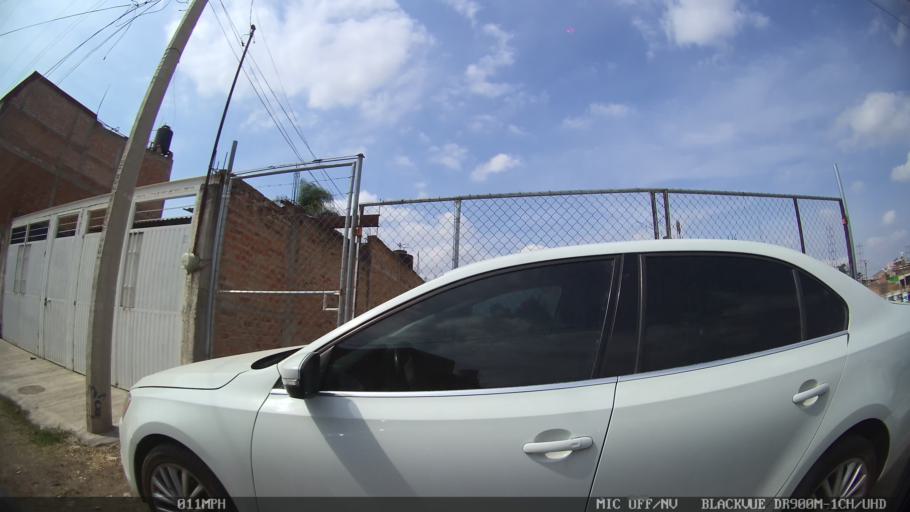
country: MX
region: Jalisco
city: Coyula
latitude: 20.6476
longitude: -103.2106
